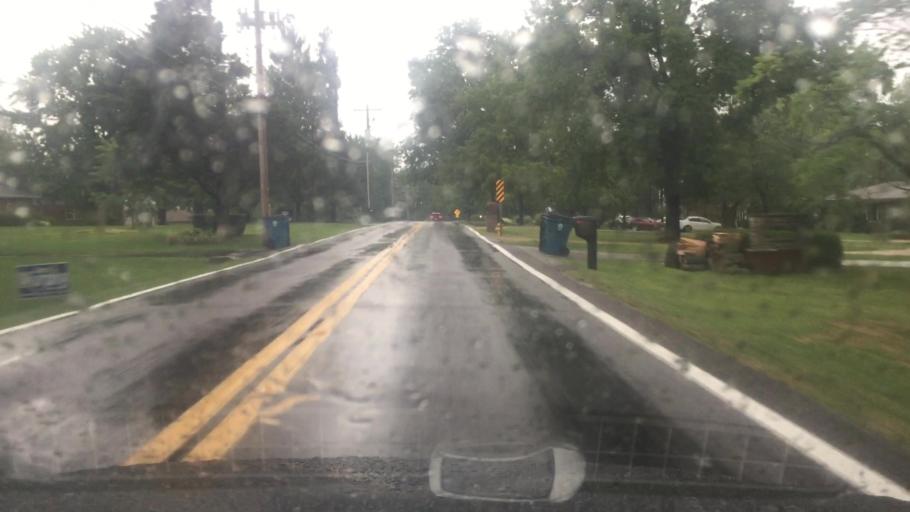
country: US
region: Missouri
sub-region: Saint Louis County
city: Concord
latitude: 38.5118
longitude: -90.3591
